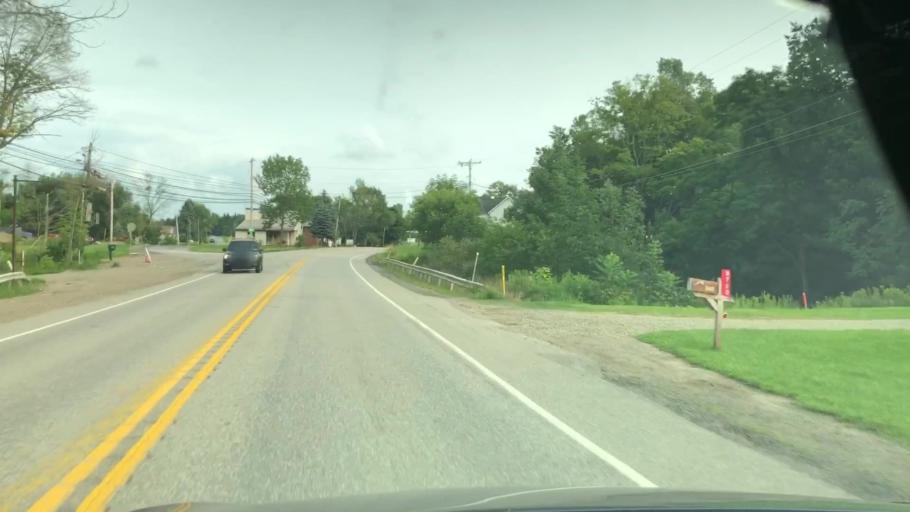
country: US
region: Pennsylvania
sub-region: Erie County
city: Wesleyville
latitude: 42.0786
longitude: -79.9877
